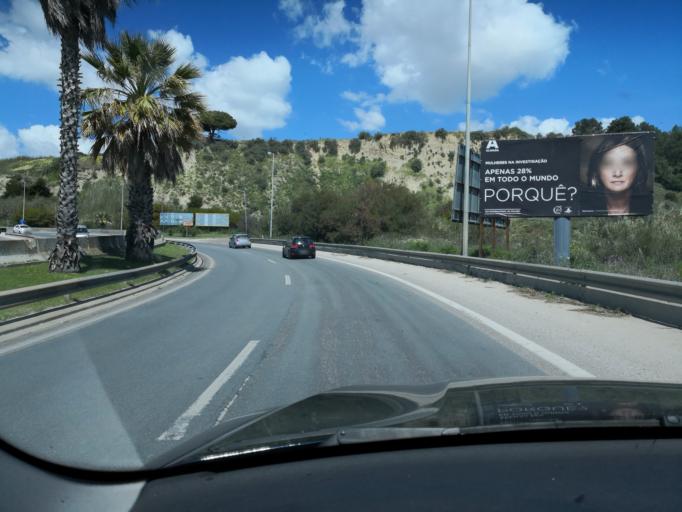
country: PT
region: Setubal
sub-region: Almada
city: Costa de Caparica
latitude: 38.6473
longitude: -9.2290
